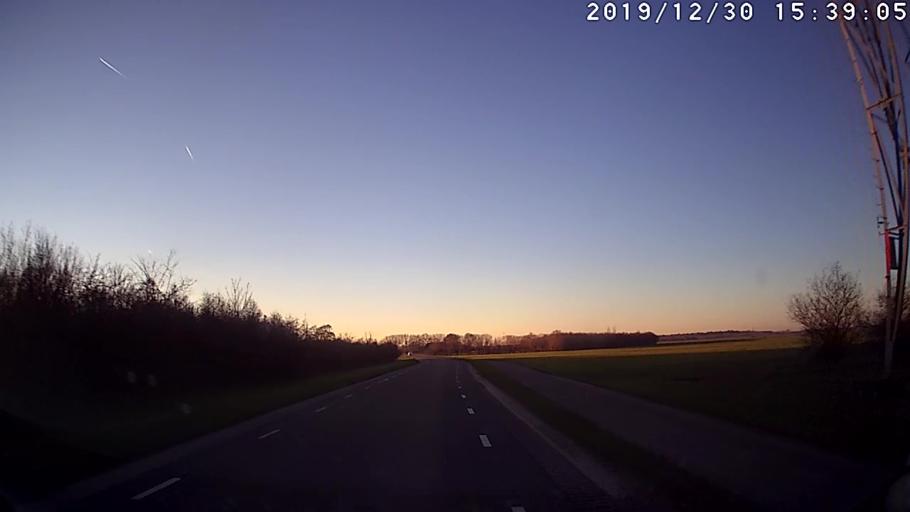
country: NL
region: Overijssel
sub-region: Gemeente Raalte
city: Heino
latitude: 52.4601
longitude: 6.1666
